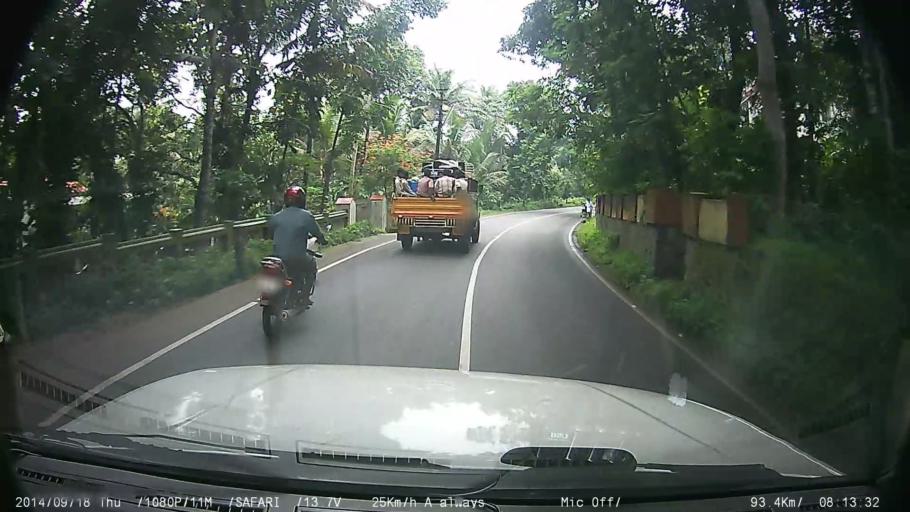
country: IN
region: Kerala
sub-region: Kottayam
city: Kottayam
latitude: 9.6159
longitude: 76.6040
